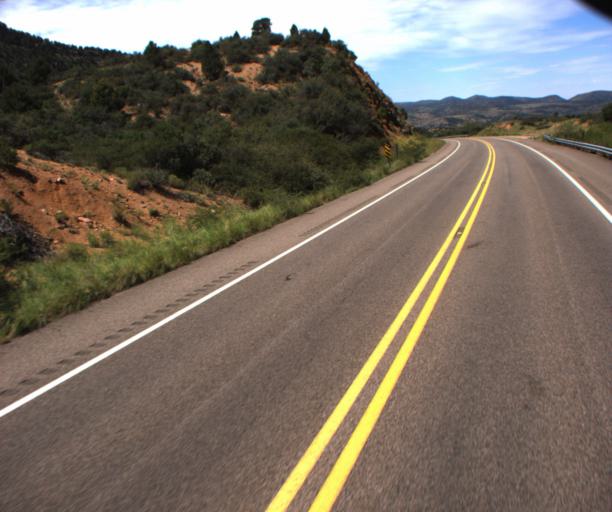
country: US
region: Arizona
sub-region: Gila County
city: Globe
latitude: 33.6125
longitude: -110.6137
